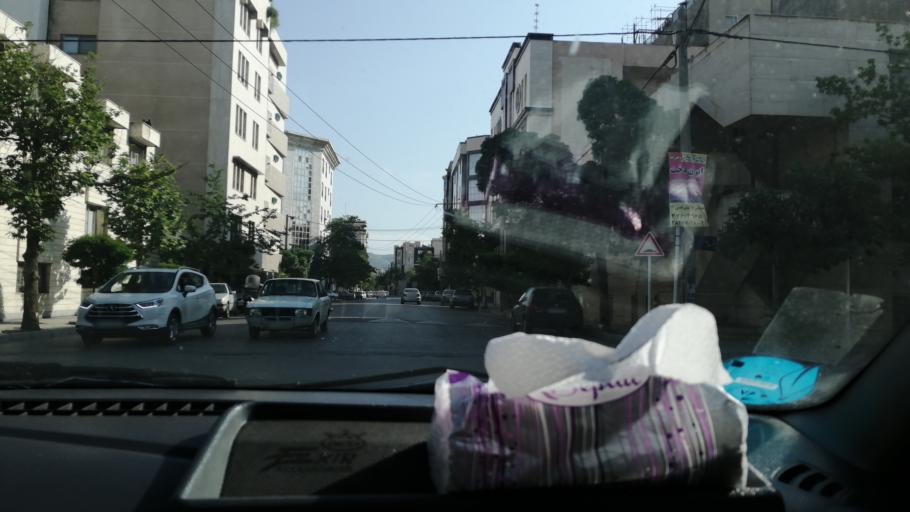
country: IR
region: Razavi Khorasan
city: Mashhad
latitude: 36.3102
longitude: 59.5610
